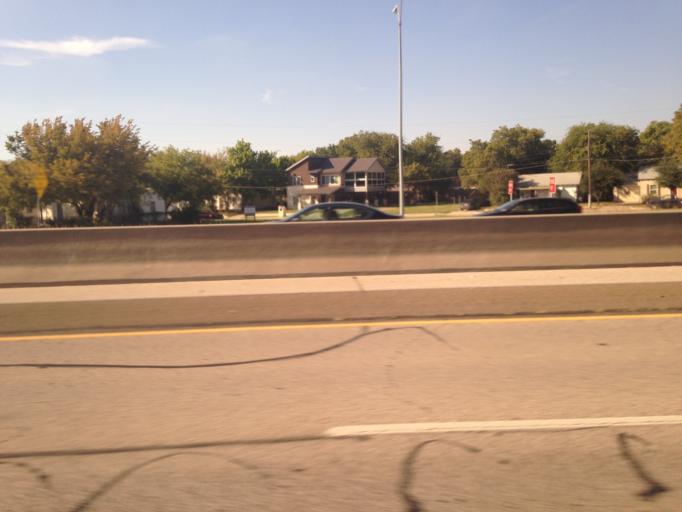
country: US
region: Texas
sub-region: Tarrant County
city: Haltom City
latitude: 32.7756
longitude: -97.2860
